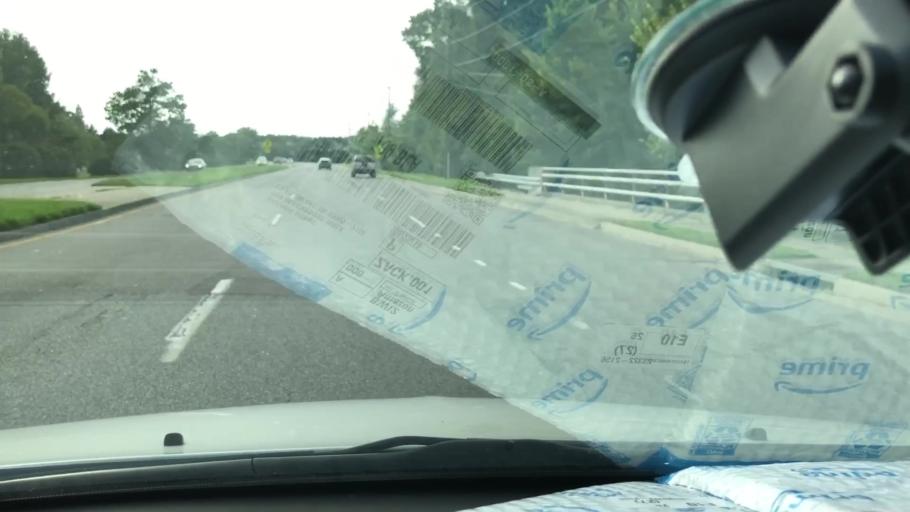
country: US
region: Virginia
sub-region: City of Chesapeake
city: Chesapeake
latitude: 36.7110
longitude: -76.2730
